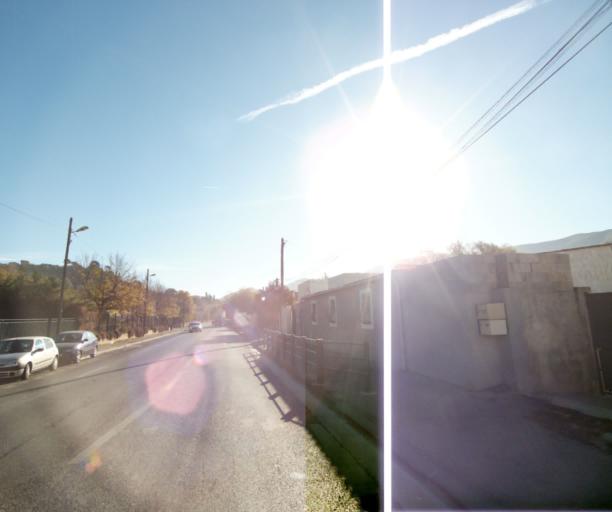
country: FR
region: Provence-Alpes-Cote d'Azur
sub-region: Departement des Bouches-du-Rhone
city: Marseille 11
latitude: 43.2918
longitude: 5.4600
